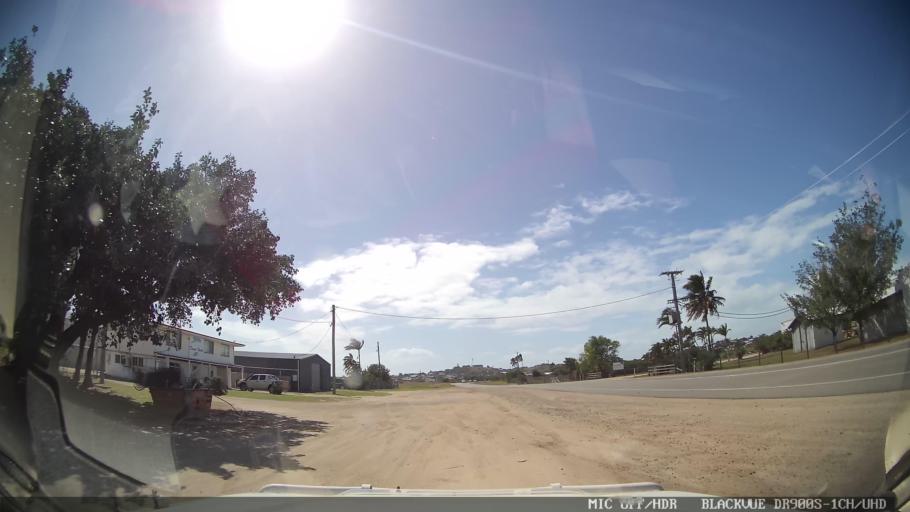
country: AU
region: Queensland
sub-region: Whitsunday
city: Bowen
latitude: -20.0129
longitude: 148.2244
